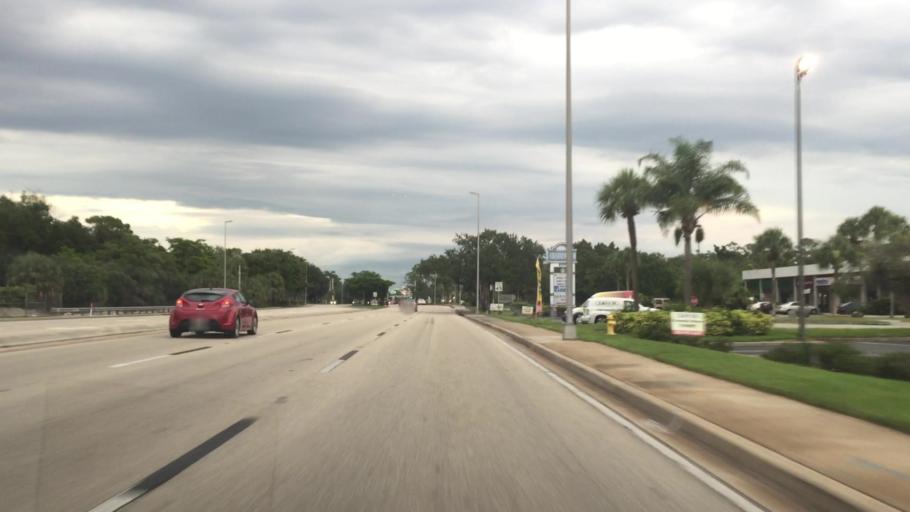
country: US
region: Florida
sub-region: Lee County
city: McGregor
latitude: 26.5566
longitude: -81.8976
